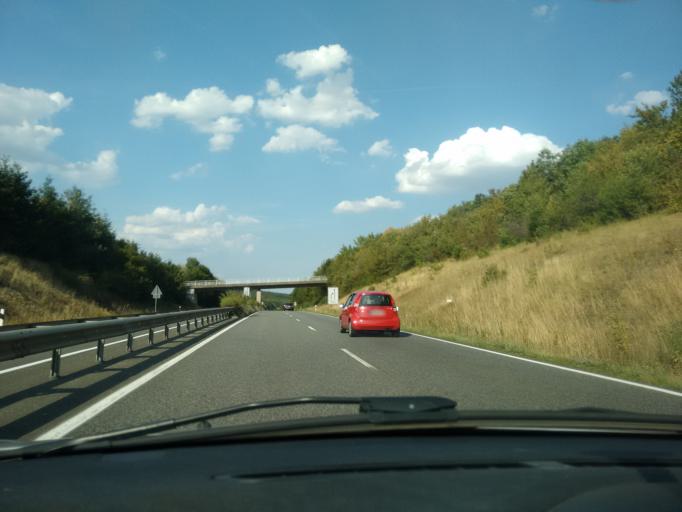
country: DE
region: Rheinland-Pfalz
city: Staudernheim
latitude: 49.8038
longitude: 7.6750
